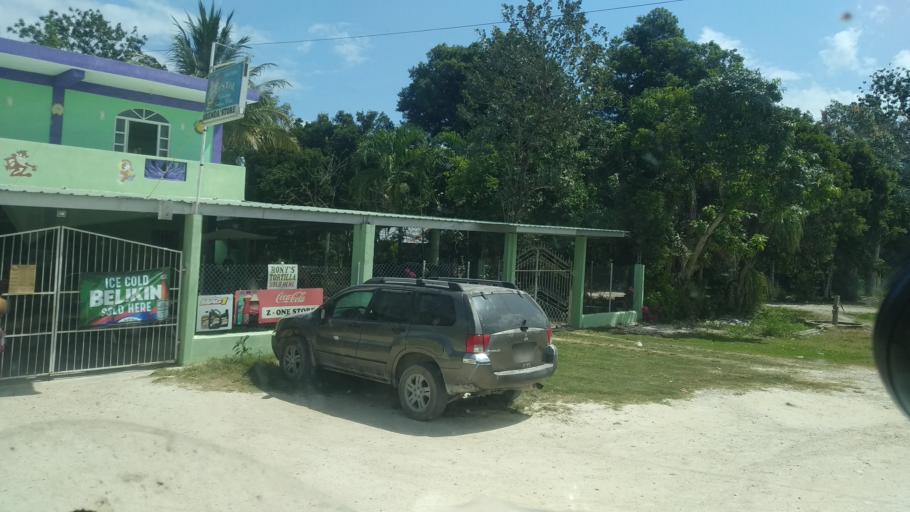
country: BZ
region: Corozal
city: Corozal
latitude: 18.3903
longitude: -88.4150
